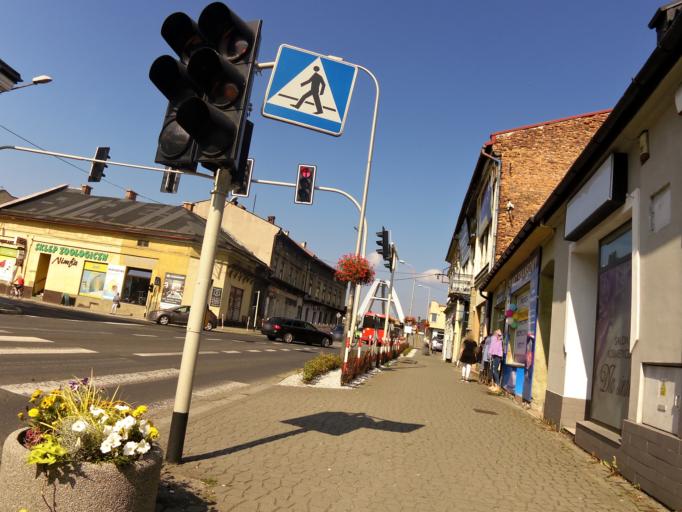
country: PL
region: Silesian Voivodeship
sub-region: Powiat zywiecki
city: Zywiec
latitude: 49.6848
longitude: 19.1918
